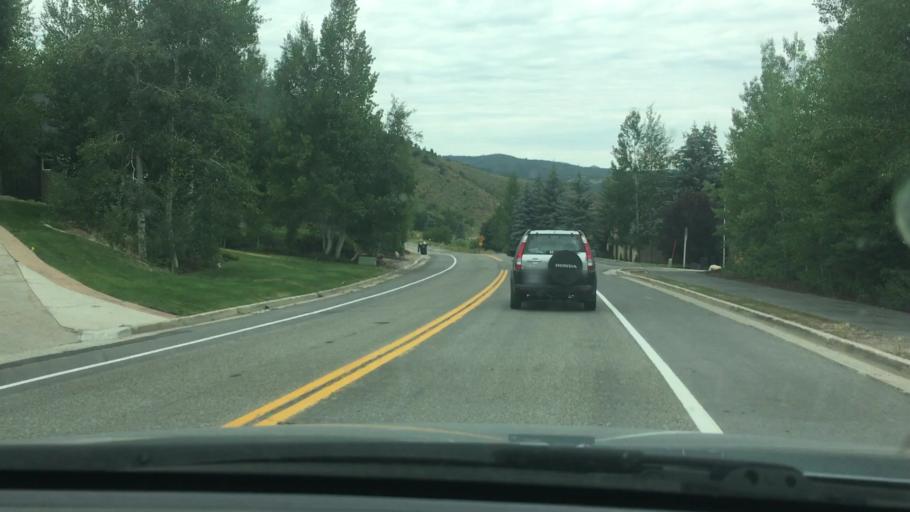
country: US
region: Utah
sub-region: Summit County
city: Summit Park
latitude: 40.7627
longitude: -111.5792
